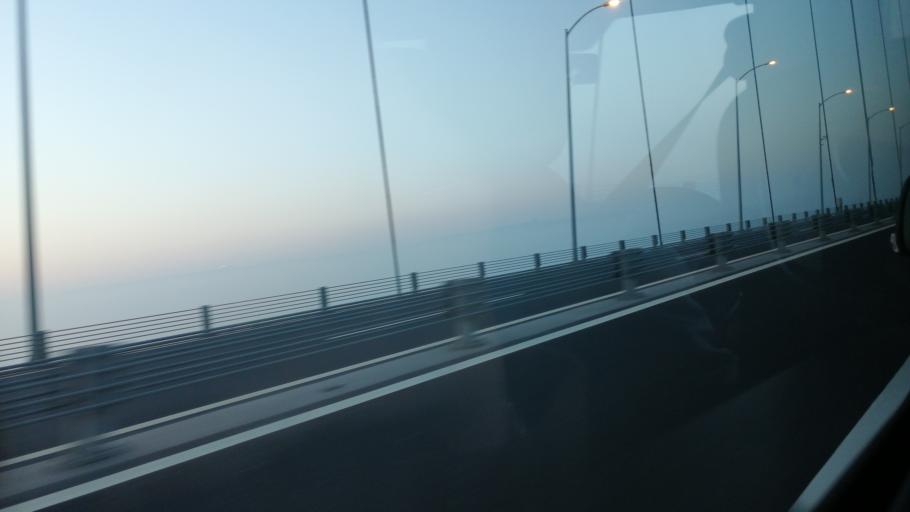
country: TR
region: Kocaeli
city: Tavsancil
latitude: 40.7573
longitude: 29.5163
